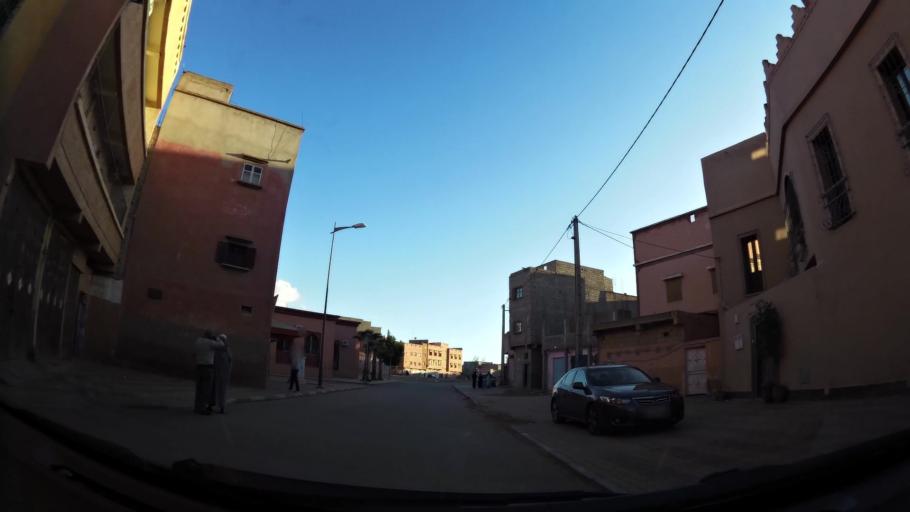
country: MA
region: Marrakech-Tensift-Al Haouz
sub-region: Kelaa-Des-Sraghna
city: Sidi Abdallah
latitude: 32.2441
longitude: -7.9529
